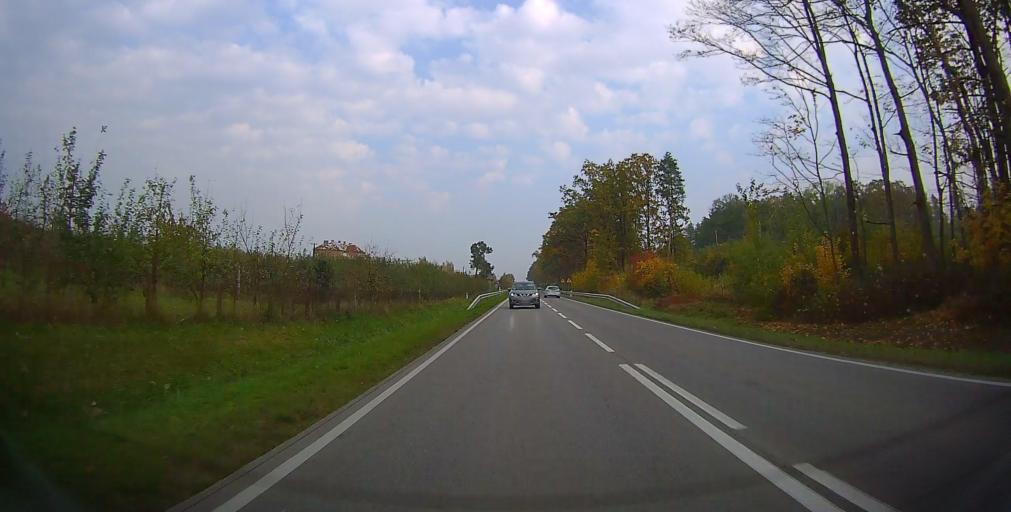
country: PL
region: Masovian Voivodeship
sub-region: Powiat grojecki
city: Belsk Duzy
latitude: 51.7934
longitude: 20.7848
